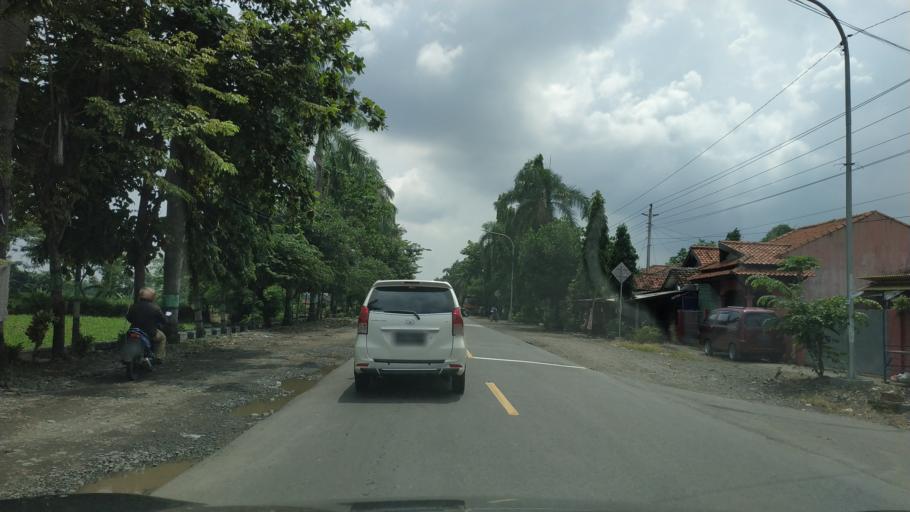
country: ID
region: Central Java
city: Lebaksiu
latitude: -7.0206
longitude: 109.1420
